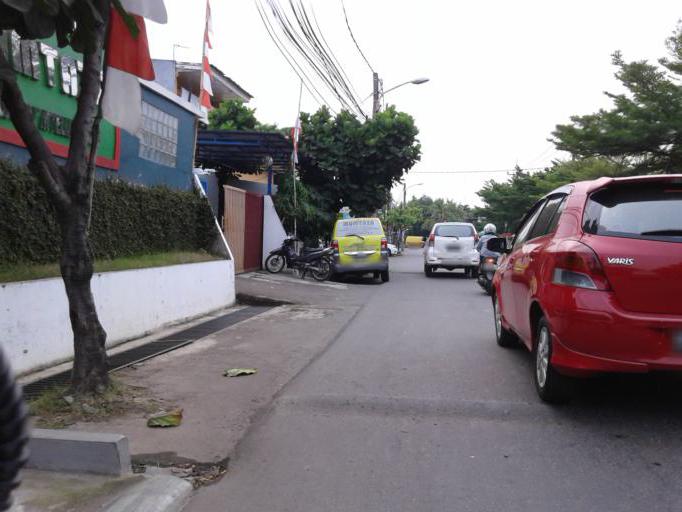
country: ID
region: West Java
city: Pamulang
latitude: -6.3239
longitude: 106.7648
